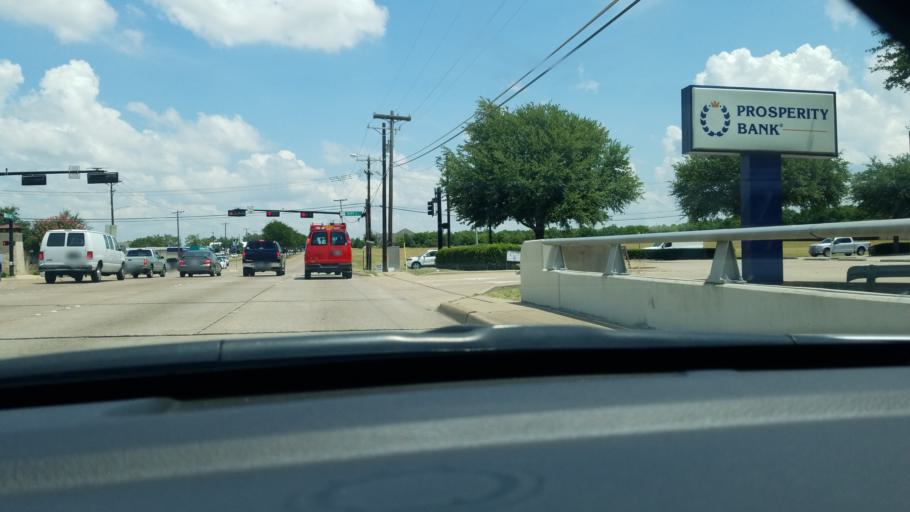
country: US
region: Texas
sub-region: Dallas County
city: Mesquite
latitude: 32.7971
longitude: -96.5957
